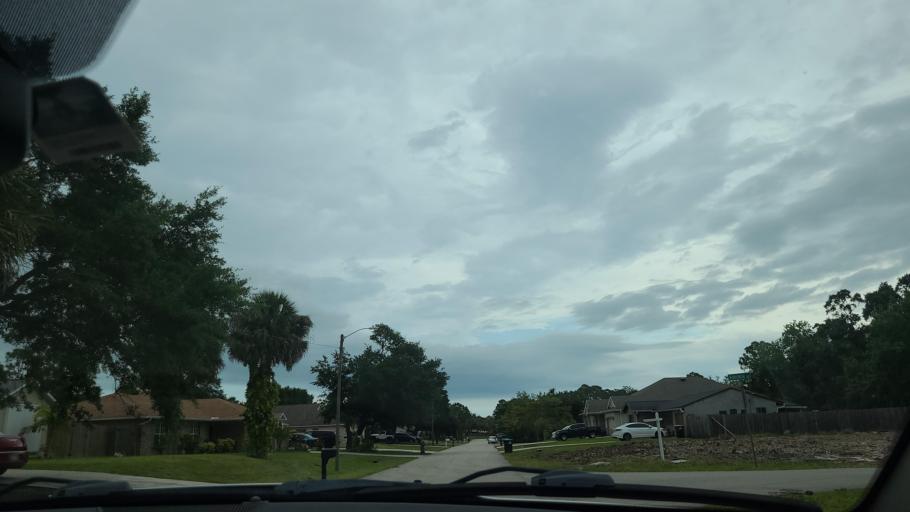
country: US
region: Florida
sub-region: Brevard County
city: West Melbourne
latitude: 28.0125
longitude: -80.6603
